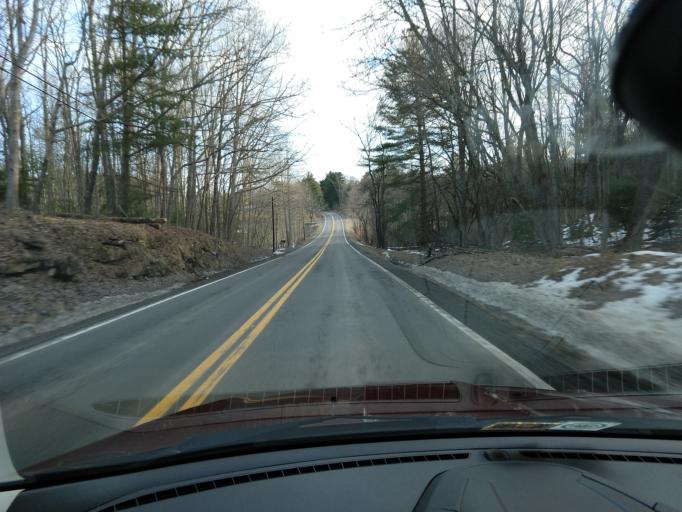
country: US
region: West Virginia
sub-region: Pocahontas County
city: Marlinton
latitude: 38.0696
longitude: -80.2895
